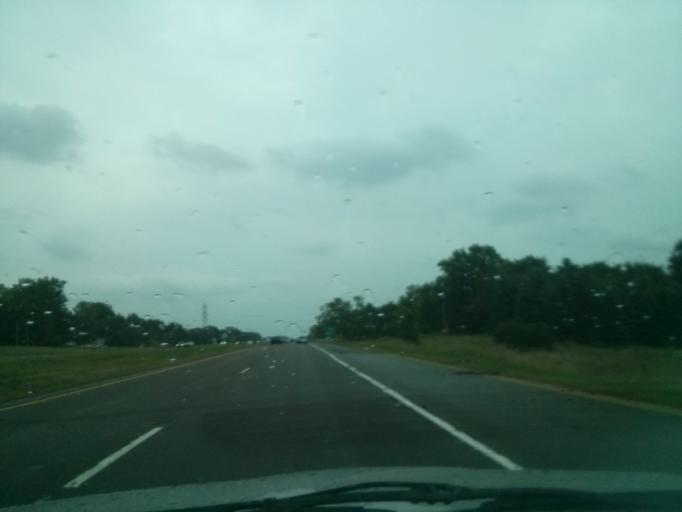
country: US
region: Minnesota
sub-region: Washington County
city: Mahtomedi
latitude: 45.0354
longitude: -92.9237
